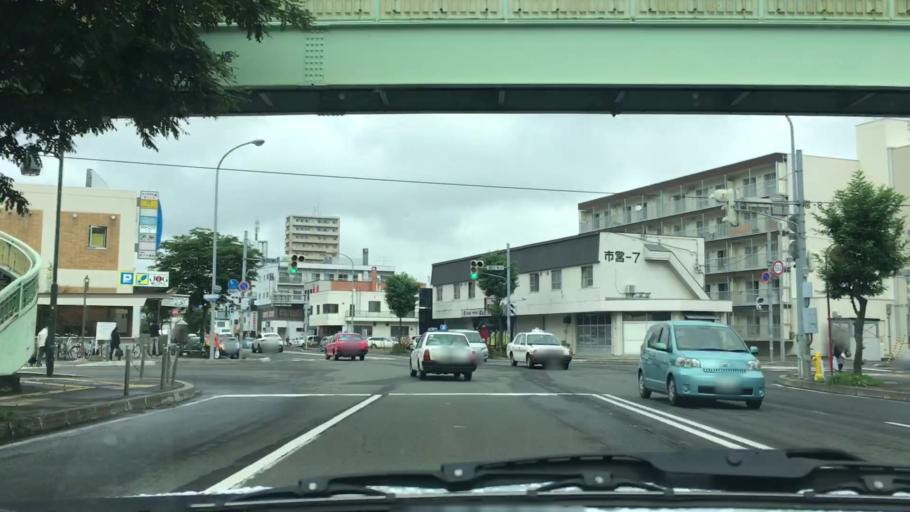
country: JP
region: Hokkaido
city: Sapporo
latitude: 43.0778
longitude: 141.3643
